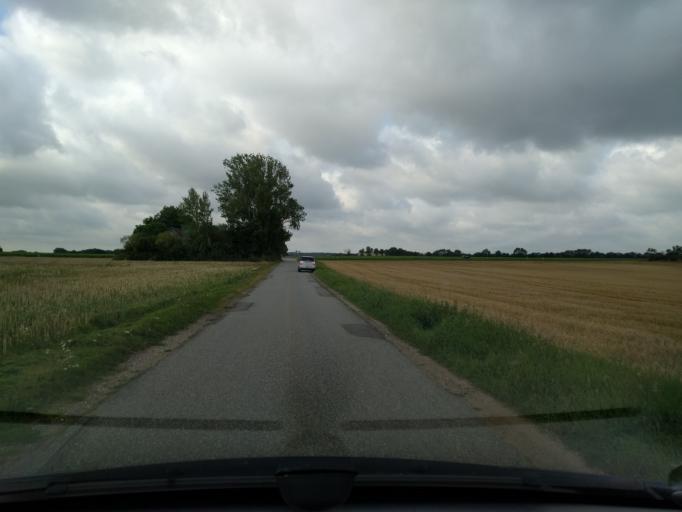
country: DK
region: Zealand
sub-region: Guldborgsund Kommune
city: Stubbekobing
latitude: 54.8963
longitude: 11.9797
